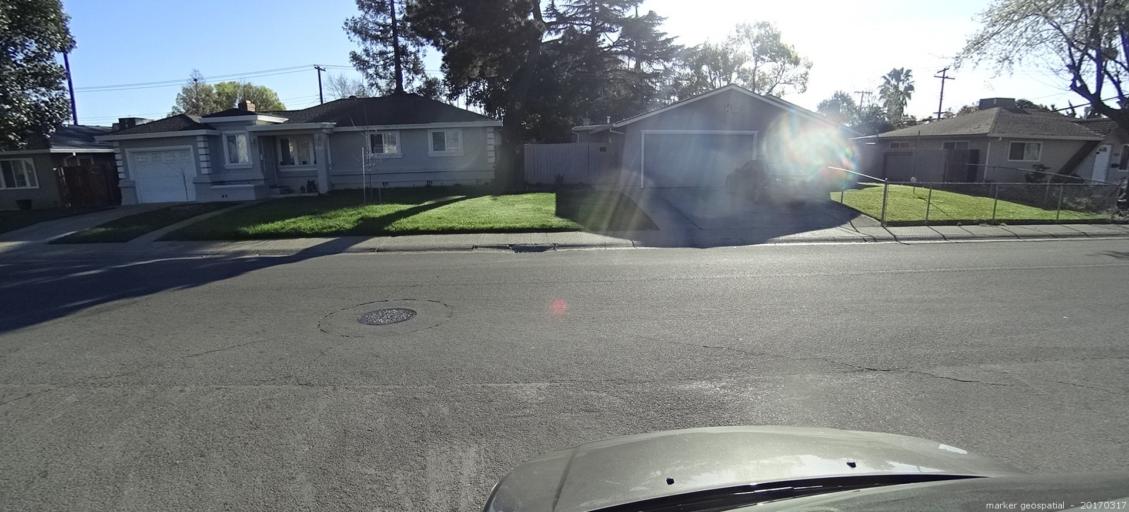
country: US
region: California
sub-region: Sacramento County
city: Parkway
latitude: 38.4922
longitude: -121.5021
